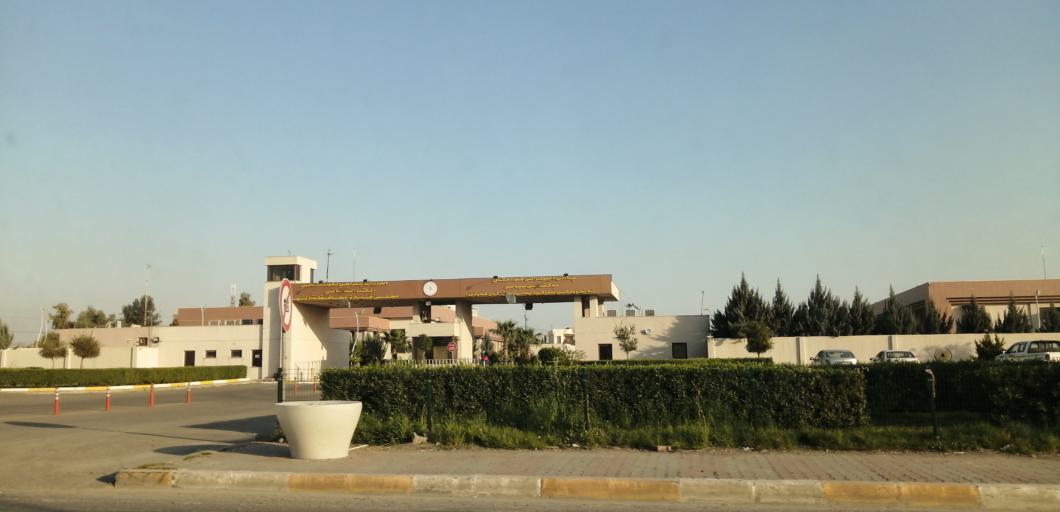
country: IQ
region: Arbil
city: Erbil
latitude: 36.2510
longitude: 44.0767
